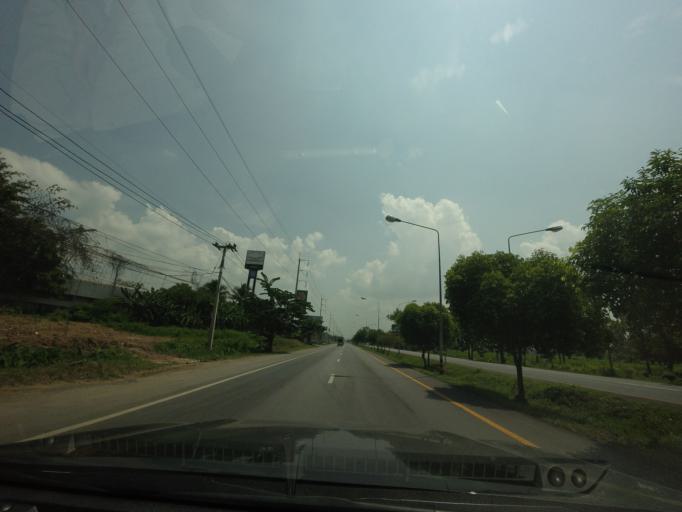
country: TH
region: Uttaradit
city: Uttaradit
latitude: 17.5856
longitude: 100.1385
